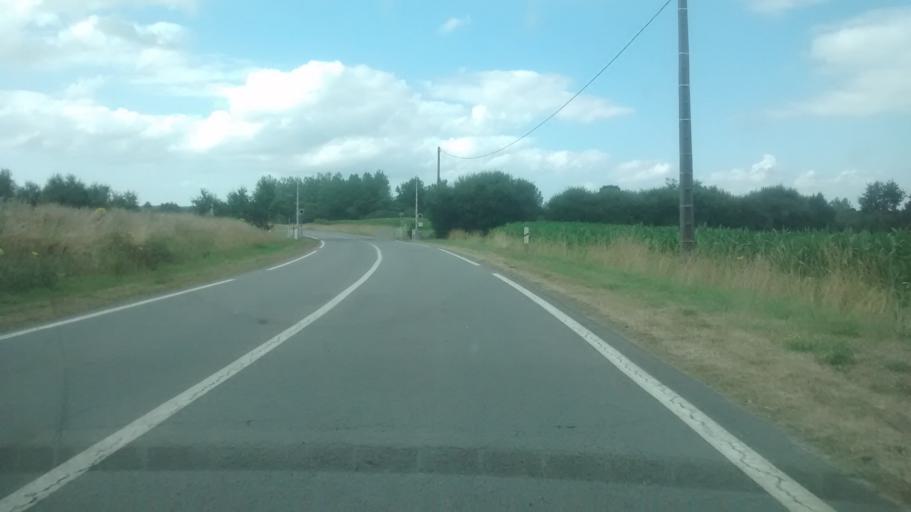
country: FR
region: Brittany
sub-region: Departement d'Ille-et-Vilaine
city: Saint-Meen-le-Grand
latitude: 48.1947
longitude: -2.1704
